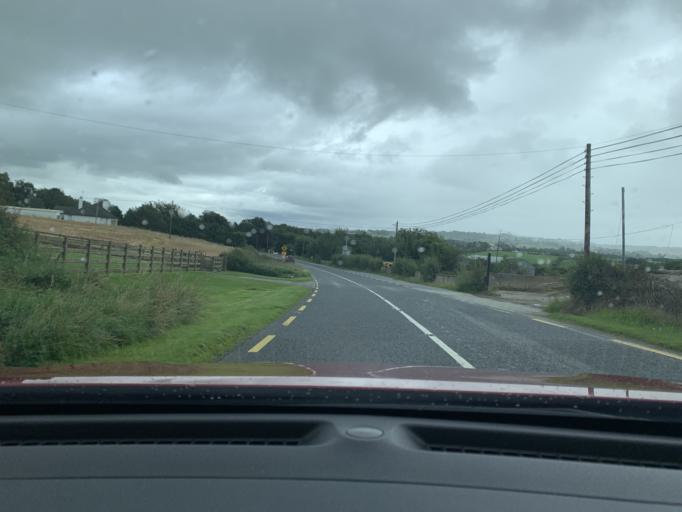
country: IE
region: Ulster
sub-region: County Donegal
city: Leifear
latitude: 54.7935
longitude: -7.5551
